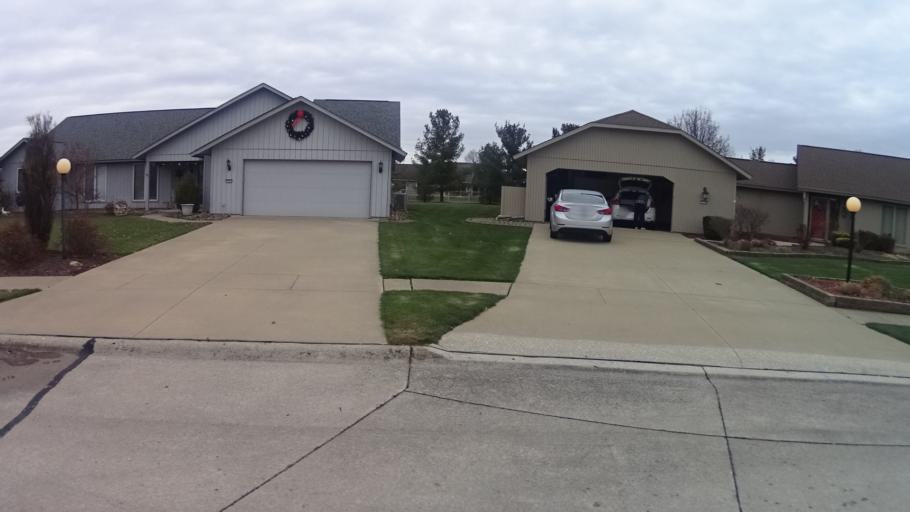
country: US
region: Ohio
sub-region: Lorain County
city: North Ridgeville
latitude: 41.3617
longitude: -81.9869
